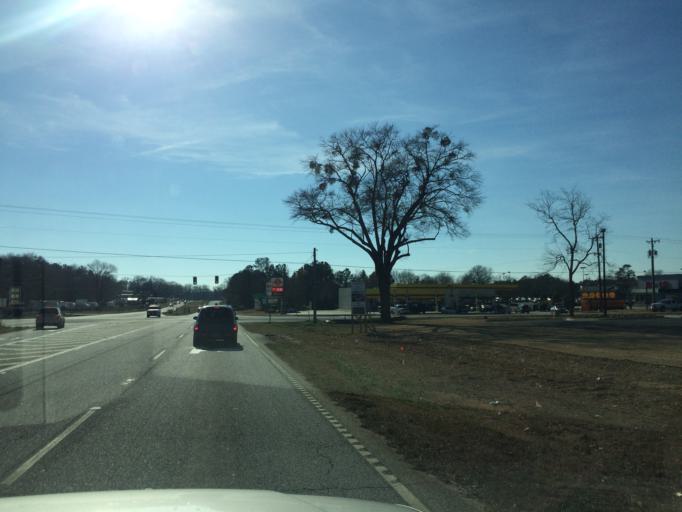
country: US
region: South Carolina
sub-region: Greenwood County
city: Greenwood
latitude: 34.2592
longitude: -82.0880
